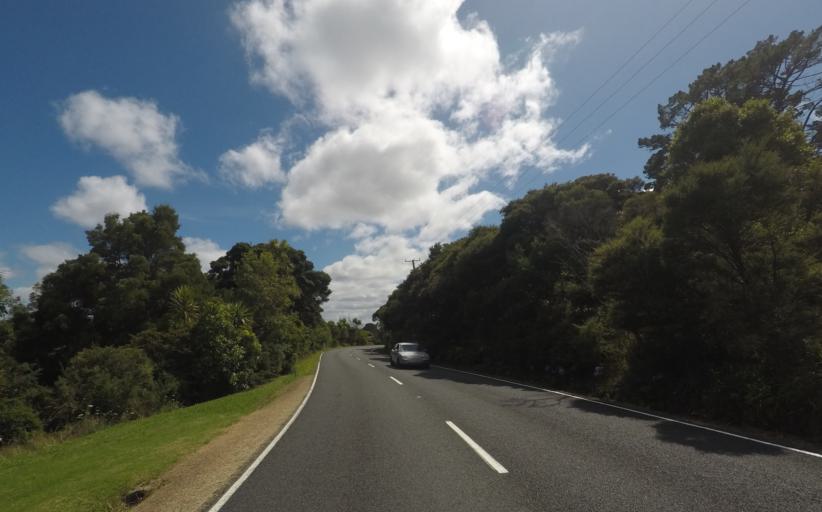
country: NZ
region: Auckland
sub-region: Auckland
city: Muriwai Beach
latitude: -36.8553
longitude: 174.5271
